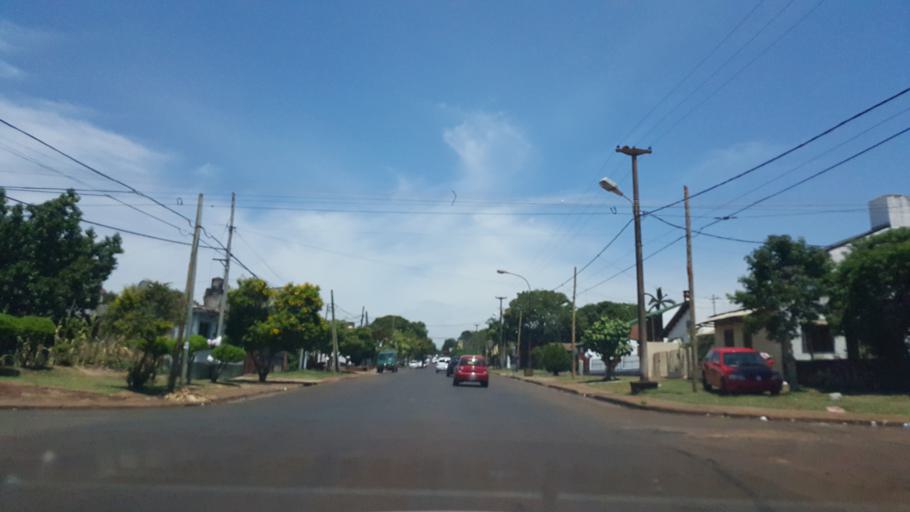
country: AR
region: Misiones
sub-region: Departamento de Capital
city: Posadas
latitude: -27.3947
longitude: -55.8980
